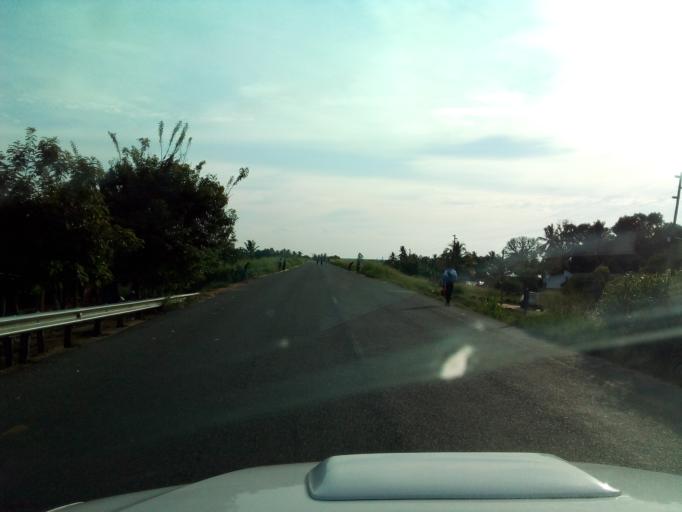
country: MZ
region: Zambezia
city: Quelimane
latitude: -17.4913
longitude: 37.0262
